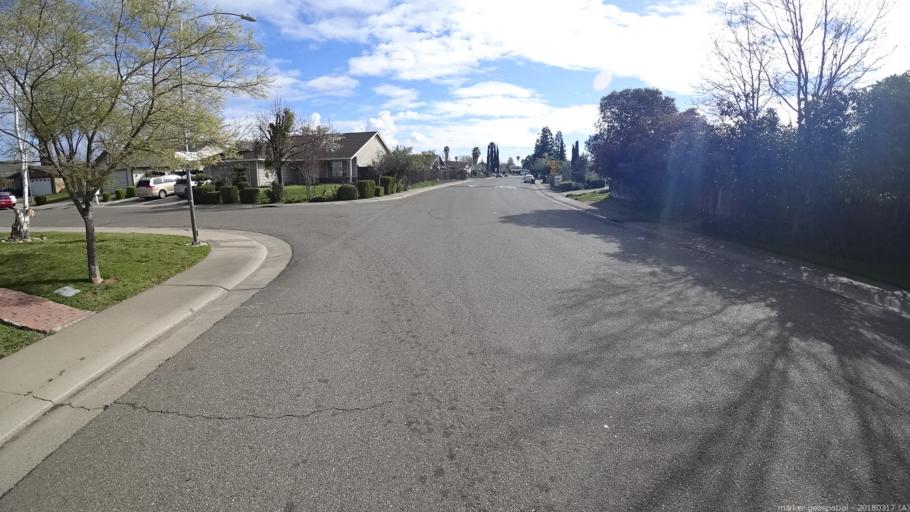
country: US
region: California
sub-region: Sacramento County
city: Florin
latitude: 38.4718
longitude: -121.4022
